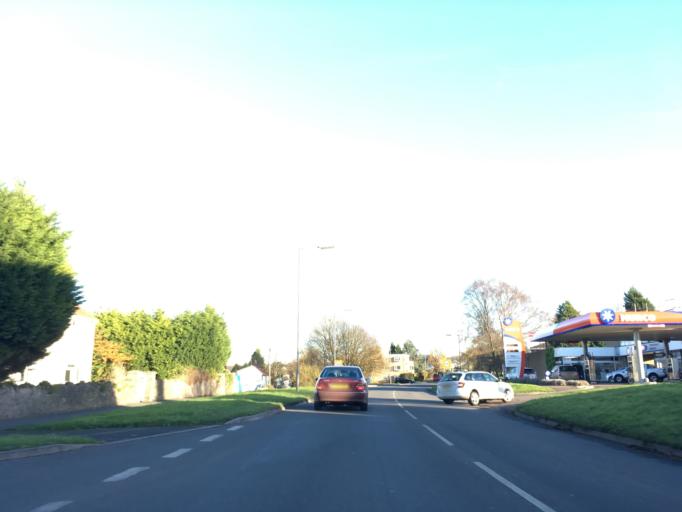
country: GB
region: England
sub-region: South Gloucestershire
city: Thornbury
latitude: 51.6071
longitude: -2.5176
